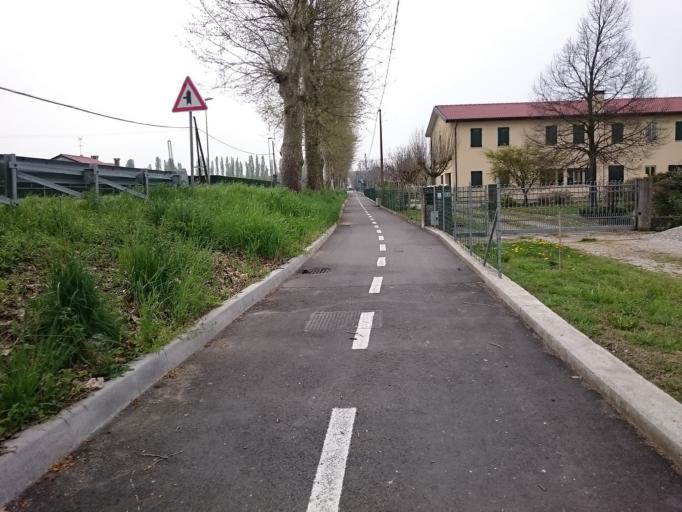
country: IT
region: Veneto
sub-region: Provincia di Padova
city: Anguillara Veneta
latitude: 45.1528
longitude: 11.8765
